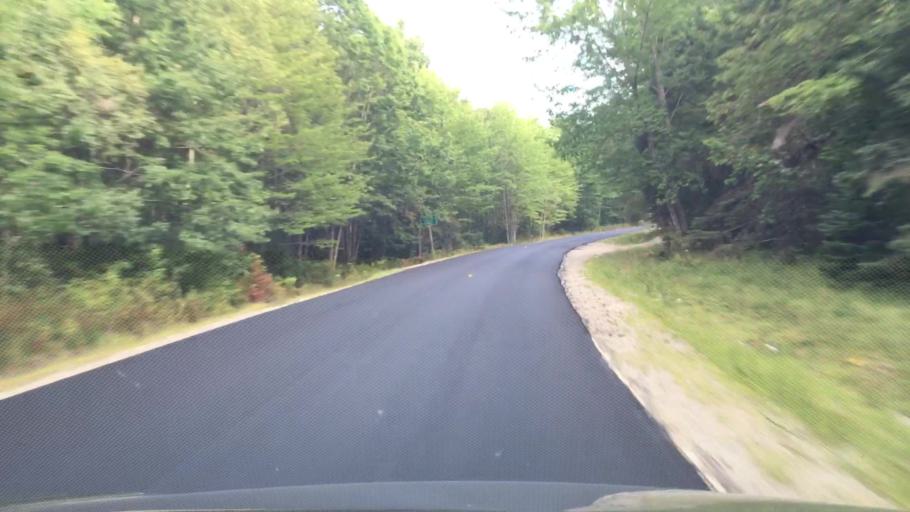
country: US
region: Maine
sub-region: Hancock County
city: Orland
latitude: 44.5436
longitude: -68.6175
